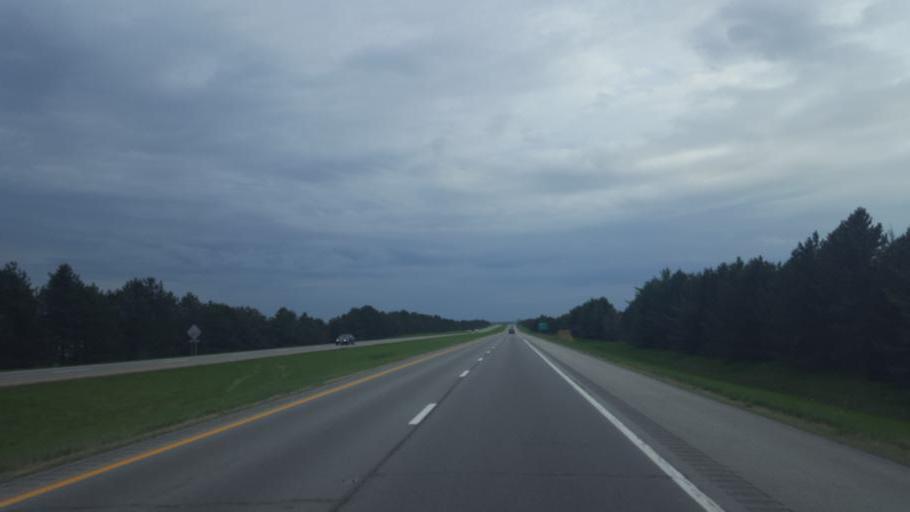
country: US
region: Ohio
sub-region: Wyandot County
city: Upper Sandusky
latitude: 40.8742
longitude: -83.3300
